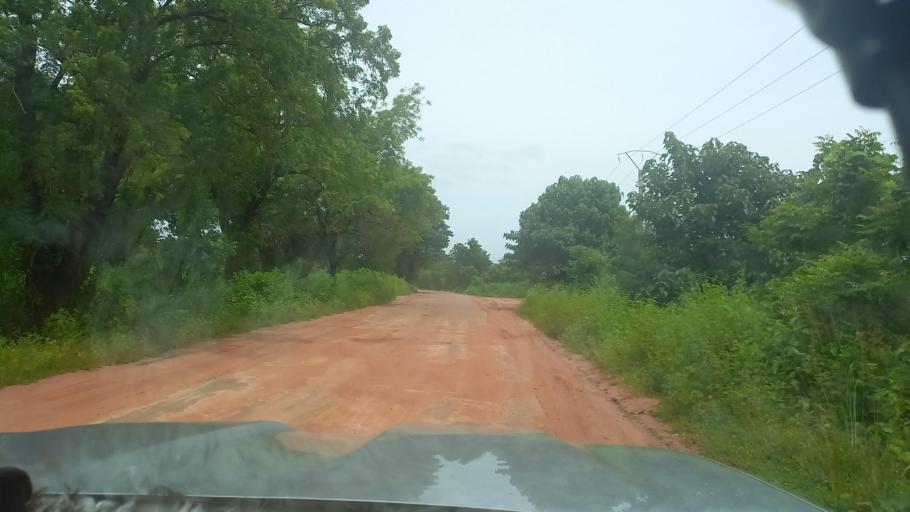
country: SN
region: Kolda
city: Marsassoum
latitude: 12.9089
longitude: -16.0128
